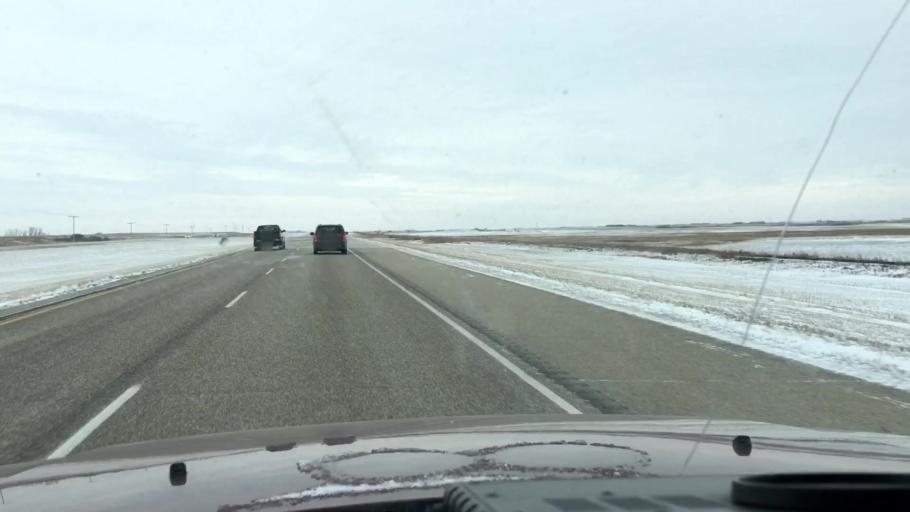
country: CA
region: Saskatchewan
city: Saskatoon
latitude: 51.5978
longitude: -106.3922
